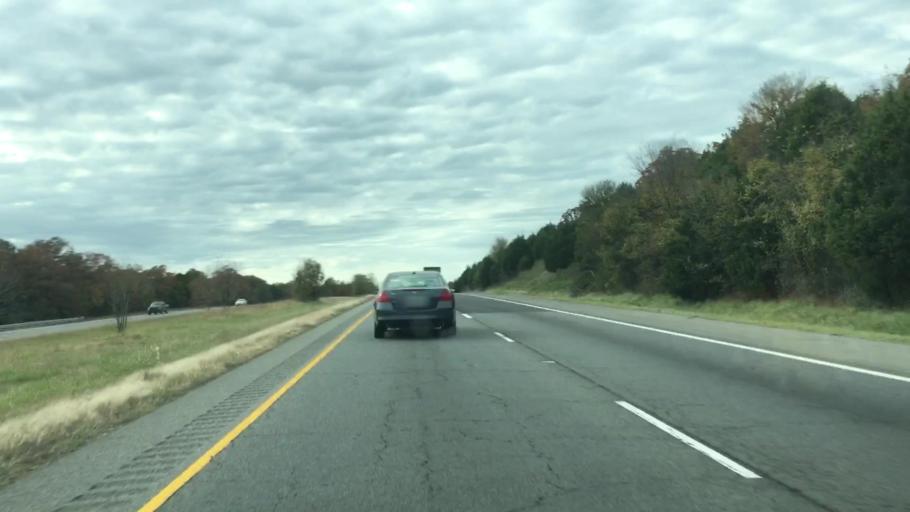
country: US
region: Arkansas
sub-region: Faulkner County
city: Conway
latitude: 35.1224
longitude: -92.4973
